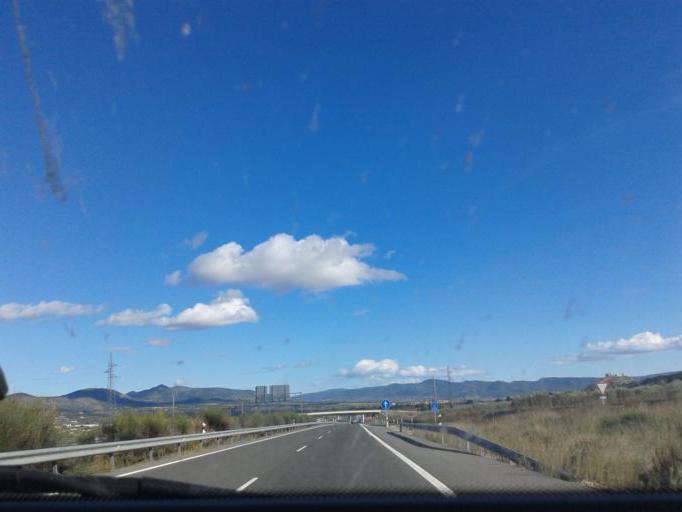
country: ES
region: Valencia
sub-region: Provincia de Alicante
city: Castalla
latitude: 38.6054
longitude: -0.7134
